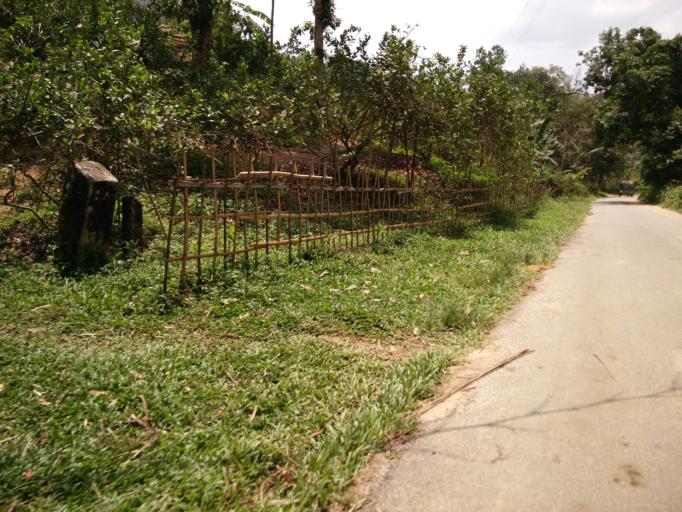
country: IN
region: Tripura
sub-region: Dhalai
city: Kamalpur
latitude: 24.3058
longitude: 91.7783
